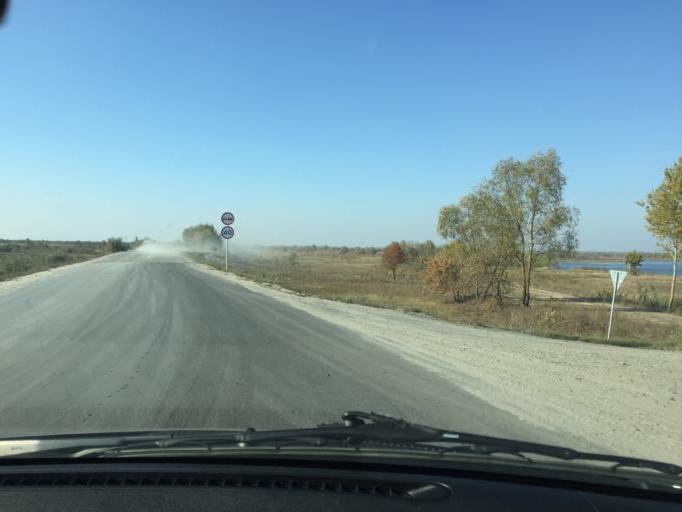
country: BY
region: Gomel
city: Turaw
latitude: 52.0675
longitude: 27.8235
